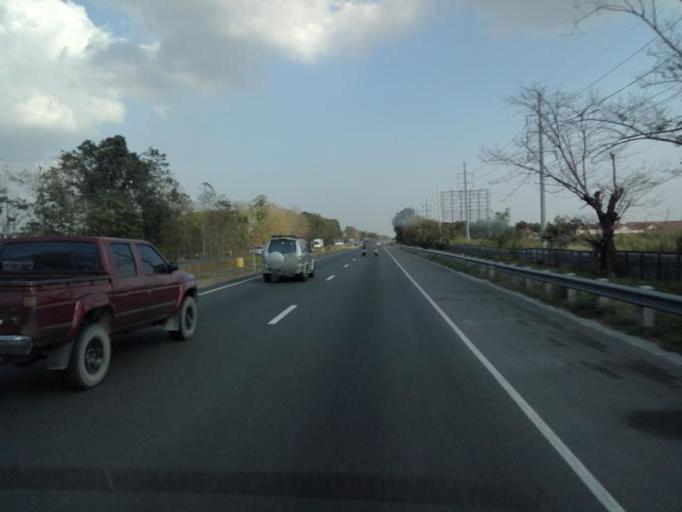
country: PH
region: Central Luzon
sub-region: Province of Pampanga
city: Acli
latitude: 15.1166
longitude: 120.6555
